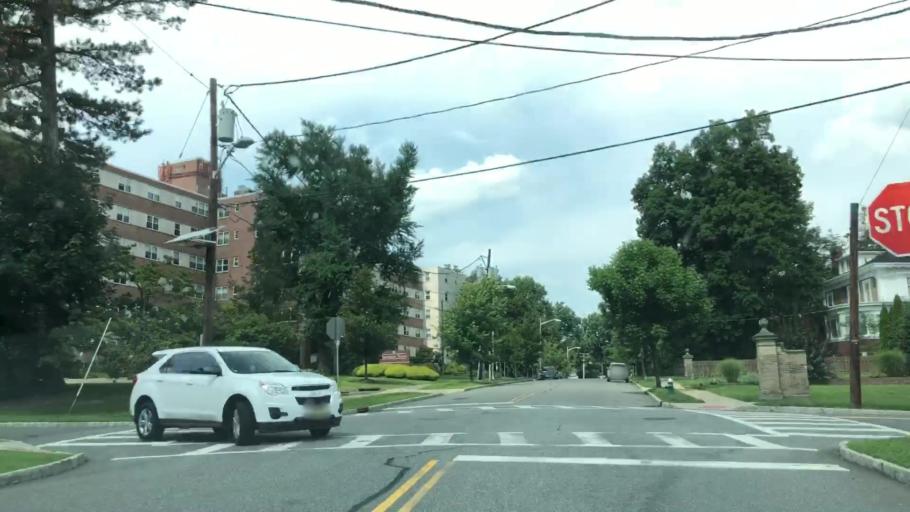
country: US
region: New Jersey
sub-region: Essex County
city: Glen Ridge
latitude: 40.8078
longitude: -74.2167
